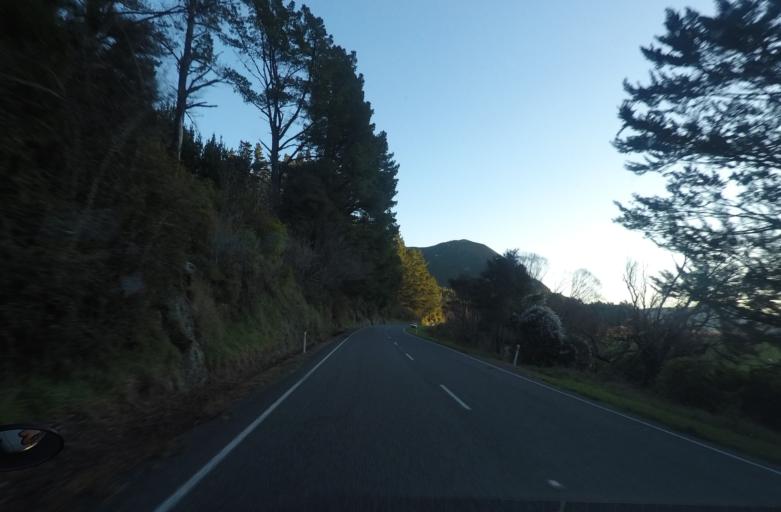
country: NZ
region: Marlborough
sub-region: Marlborough District
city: Picton
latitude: -41.2866
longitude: 173.7077
